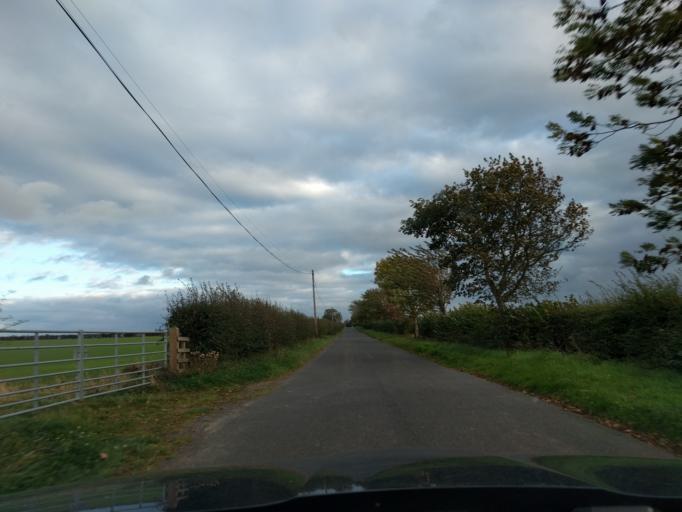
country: GB
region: England
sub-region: Northumberland
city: Ford
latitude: 55.7389
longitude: -2.1043
